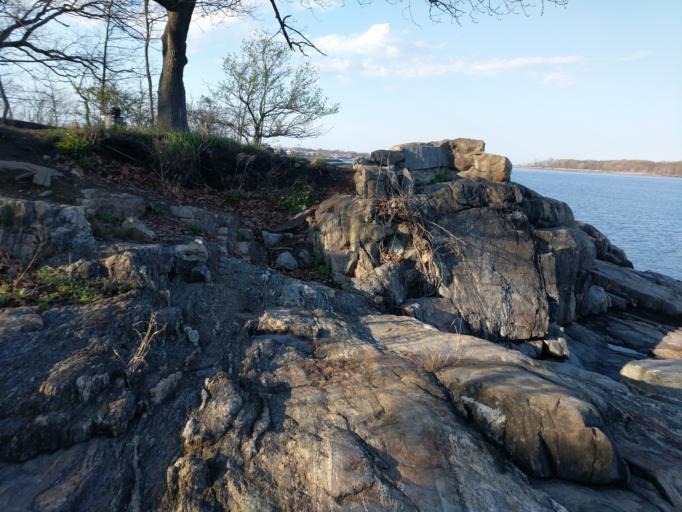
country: US
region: New York
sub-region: Westchester County
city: Pelham Manor
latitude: 40.8773
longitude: -73.7846
